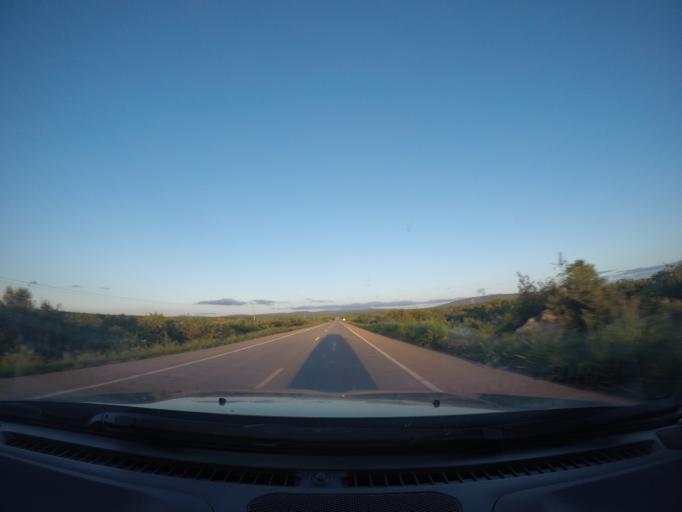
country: BR
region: Bahia
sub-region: Seabra
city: Seabra
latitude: -12.3988
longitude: -41.9395
